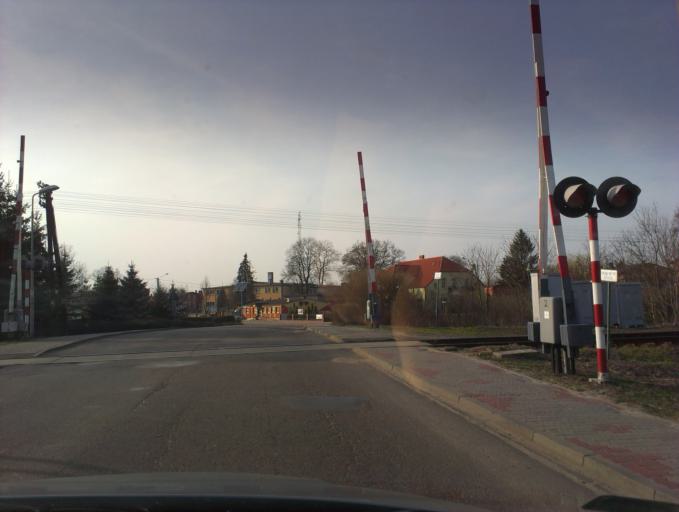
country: PL
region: Greater Poland Voivodeship
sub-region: Powiat zlotowski
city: Lipka
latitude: 53.4952
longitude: 17.2547
